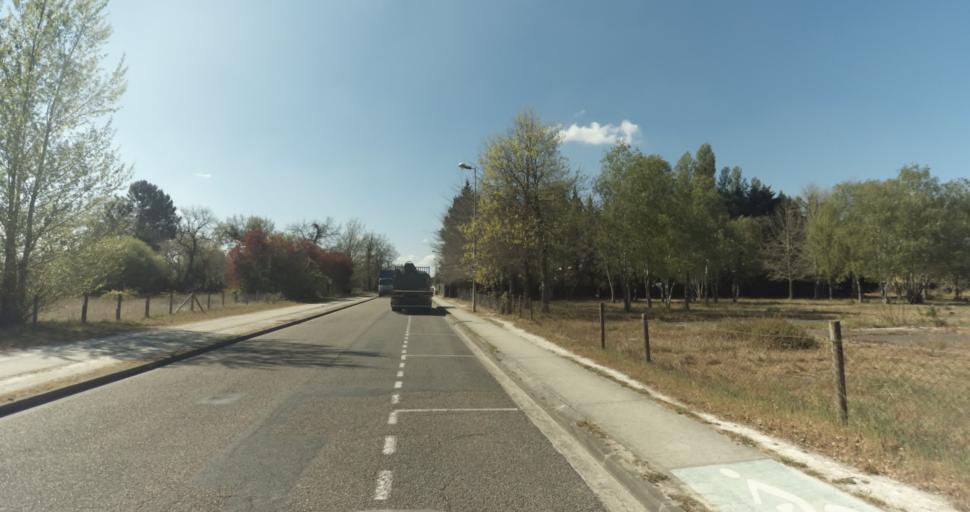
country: FR
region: Aquitaine
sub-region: Departement de la Gironde
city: Martignas-sur-Jalle
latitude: 44.8085
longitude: -0.7842
